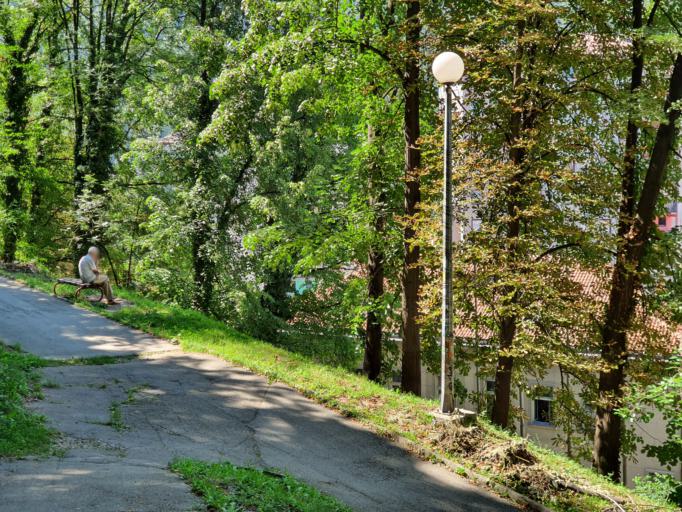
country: RS
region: Central Serbia
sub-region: Zlatiborski Okrug
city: Uzice
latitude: 43.8545
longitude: 19.8473
